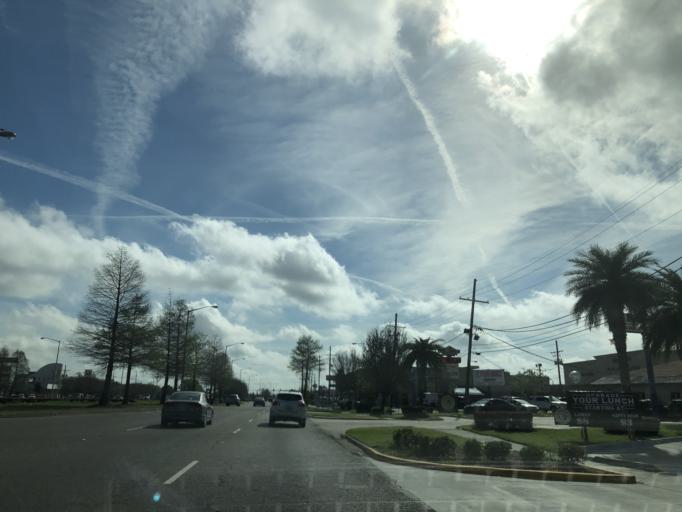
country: US
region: Louisiana
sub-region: Jefferson Parish
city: Metairie Terrace
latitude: 30.0057
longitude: -90.1983
